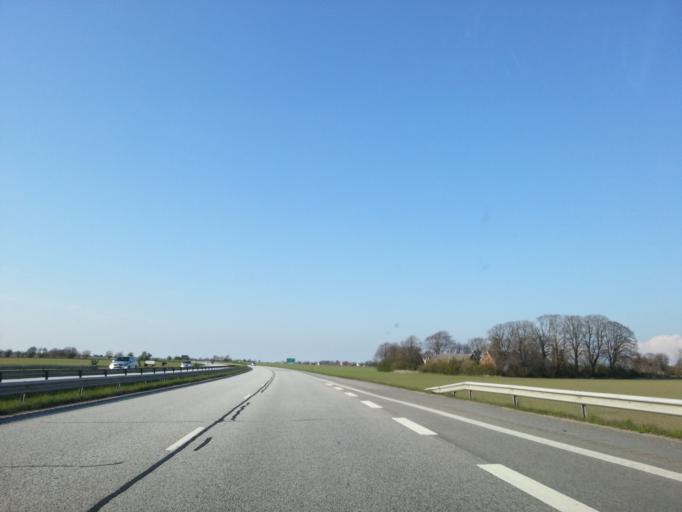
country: SE
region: Skane
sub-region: Vellinge Kommun
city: Vellinge
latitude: 55.4869
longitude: 13.0209
